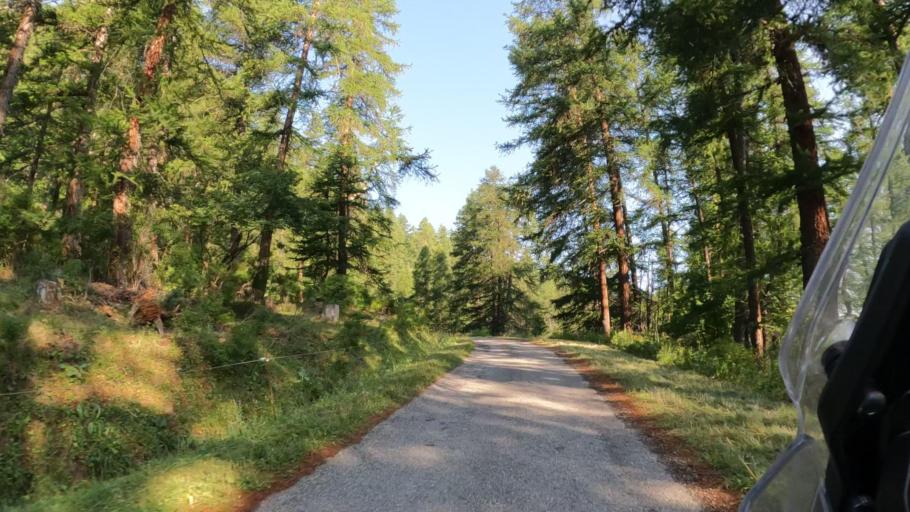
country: FR
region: Provence-Alpes-Cote d'Azur
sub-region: Departement des Hautes-Alpes
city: Guillestre
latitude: 44.6053
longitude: 6.6752
